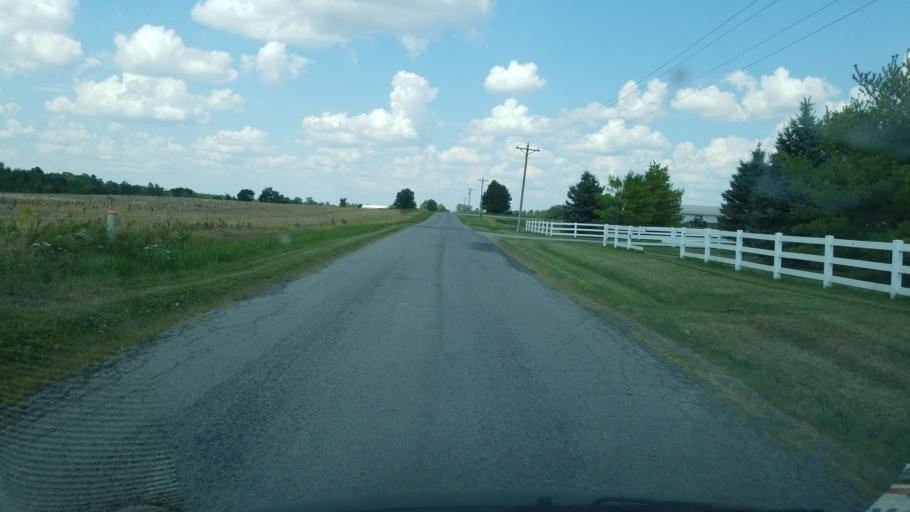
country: US
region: Ohio
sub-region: Champaign County
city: North Lewisburg
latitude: 40.3809
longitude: -83.4775
